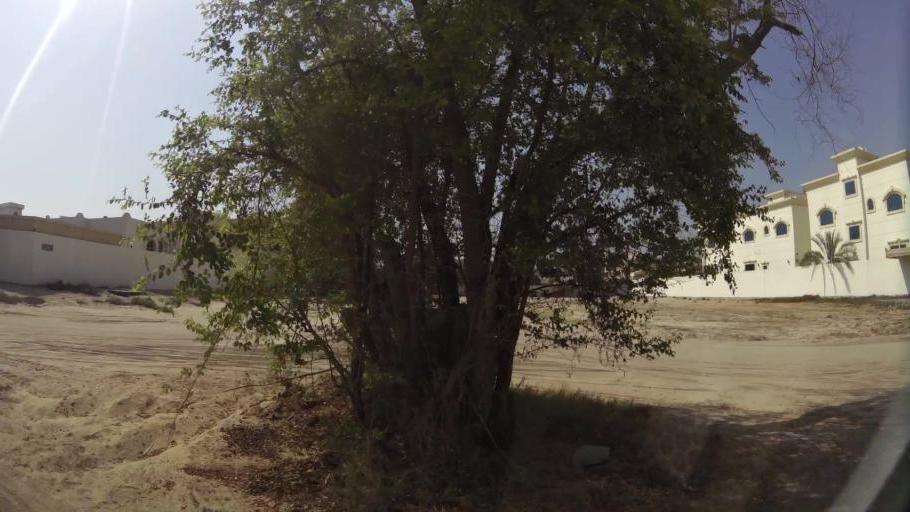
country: AE
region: Ajman
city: Ajman
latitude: 25.3870
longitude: 55.4179
